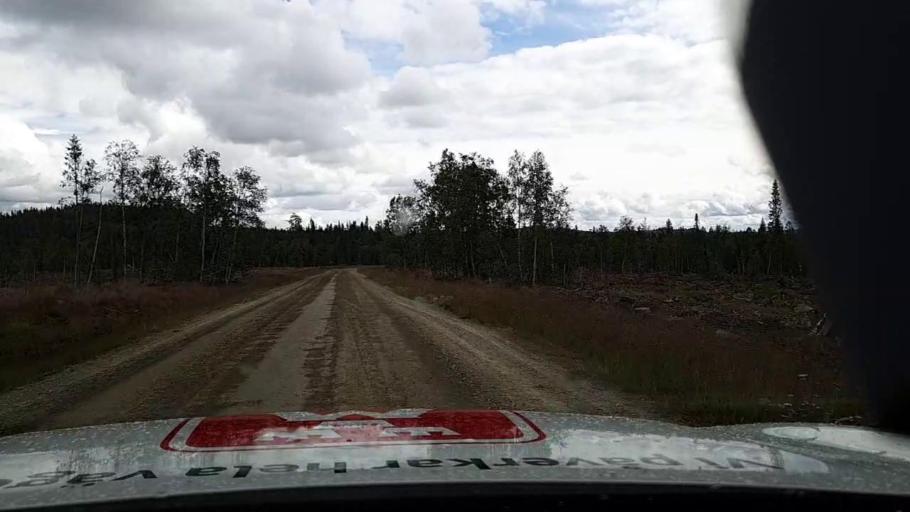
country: SE
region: Jaemtland
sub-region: Are Kommun
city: Jarpen
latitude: 62.6096
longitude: 13.2066
